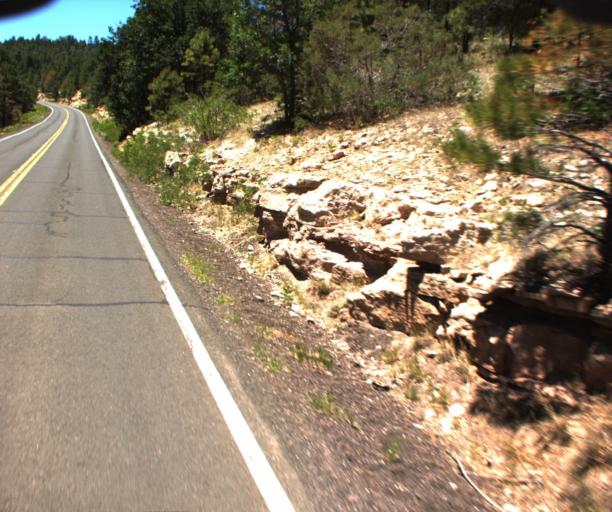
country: US
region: Arizona
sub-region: Gila County
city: Pine
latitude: 34.6051
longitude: -111.2346
